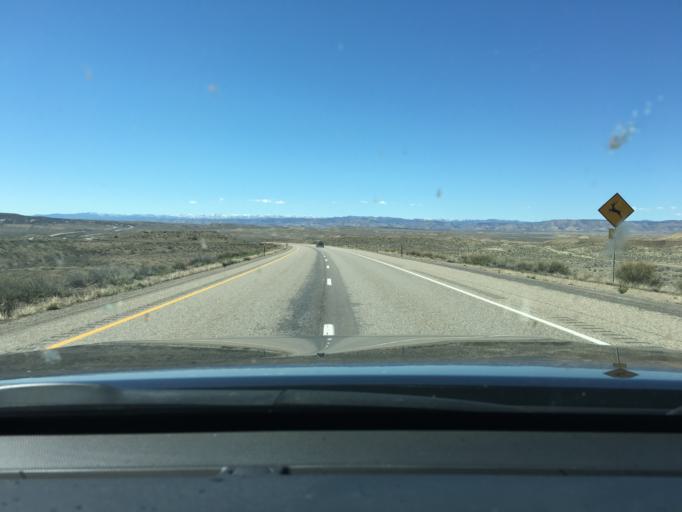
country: US
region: Colorado
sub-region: Mesa County
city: Loma
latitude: 39.1950
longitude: -109.0548
